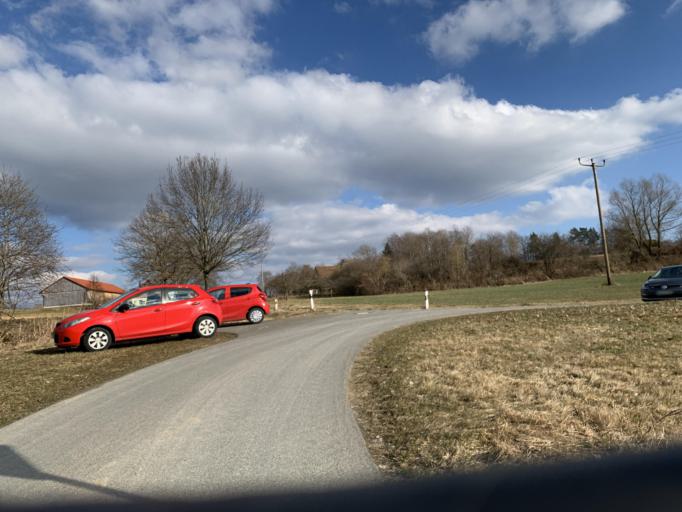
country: DE
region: Bavaria
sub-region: Upper Palatinate
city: Thanstein
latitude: 49.3762
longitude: 12.4412
